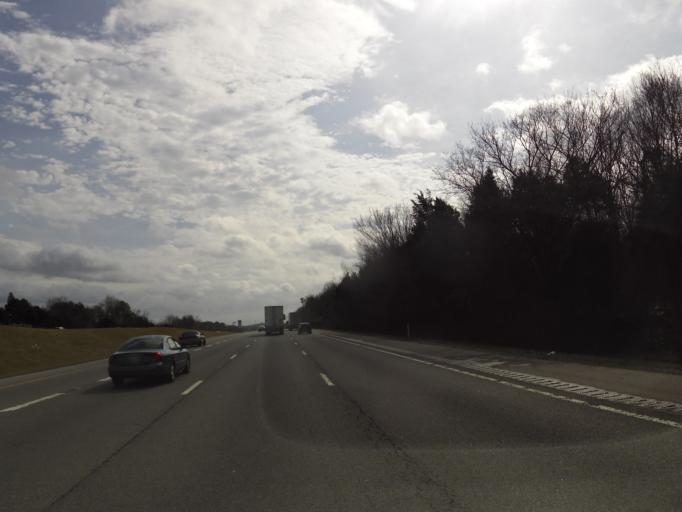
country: US
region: Tennessee
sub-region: Rutherford County
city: Smyrna
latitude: 35.9441
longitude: -86.5430
